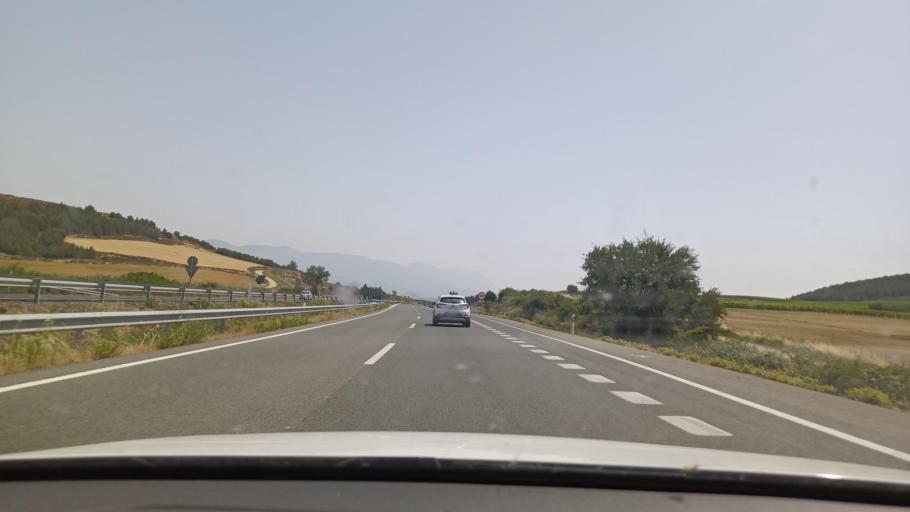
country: ES
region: La Rioja
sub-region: Provincia de La Rioja
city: Gimileo
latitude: 42.5366
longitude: -2.8223
